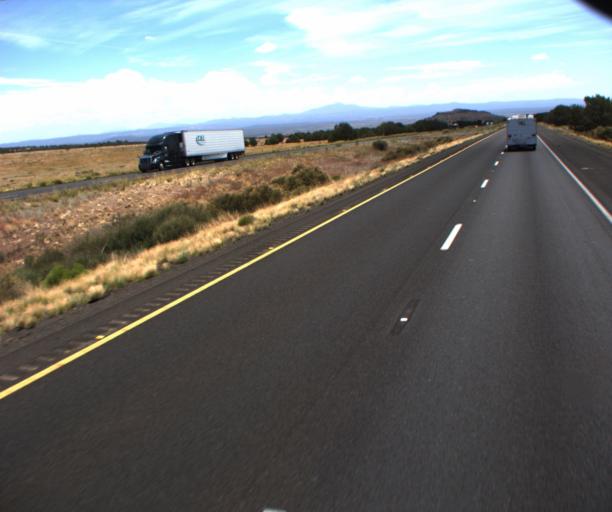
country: US
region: Arizona
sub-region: Yavapai County
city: Paulden
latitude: 35.2574
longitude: -112.7111
